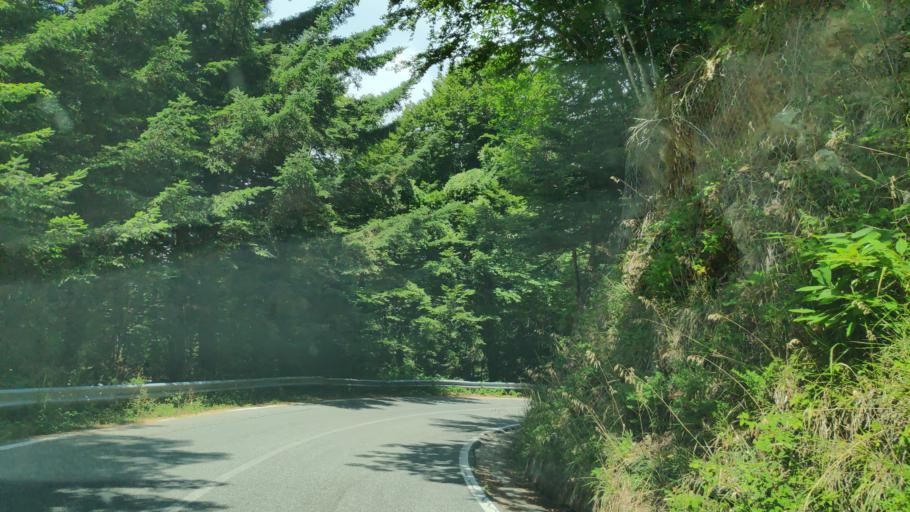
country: IT
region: Calabria
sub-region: Provincia di Vibo-Valentia
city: Mongiana
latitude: 38.5274
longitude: 16.3337
